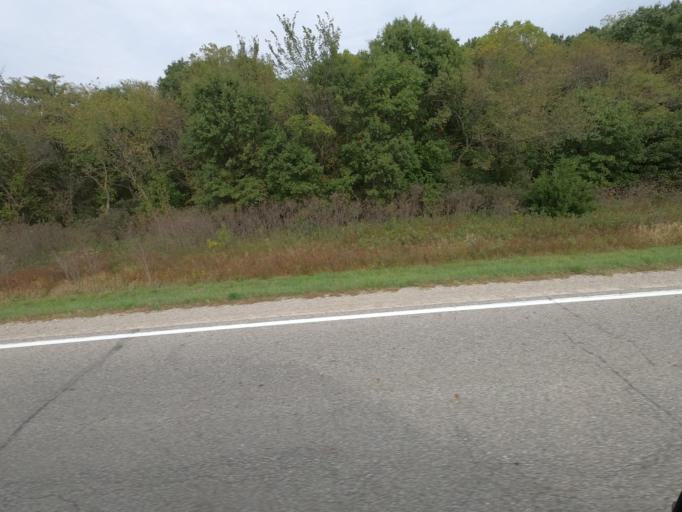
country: US
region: Iowa
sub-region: Jefferson County
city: Fairfield
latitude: 40.8842
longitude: -92.1627
